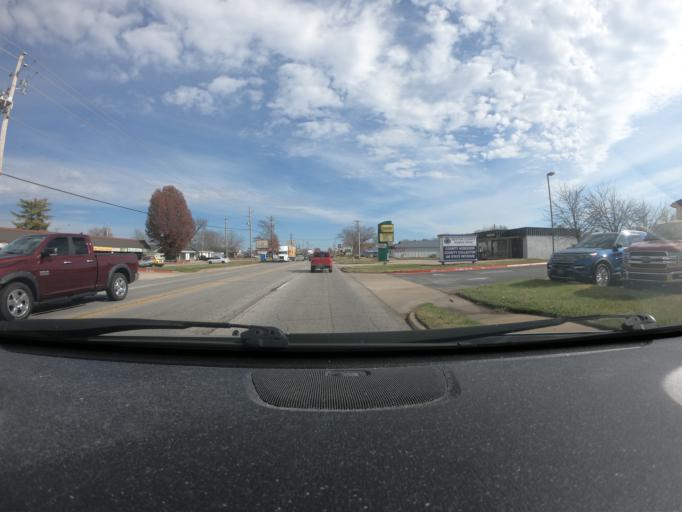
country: US
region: Arkansas
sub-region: Benton County
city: Rogers
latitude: 36.3339
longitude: -94.1390
